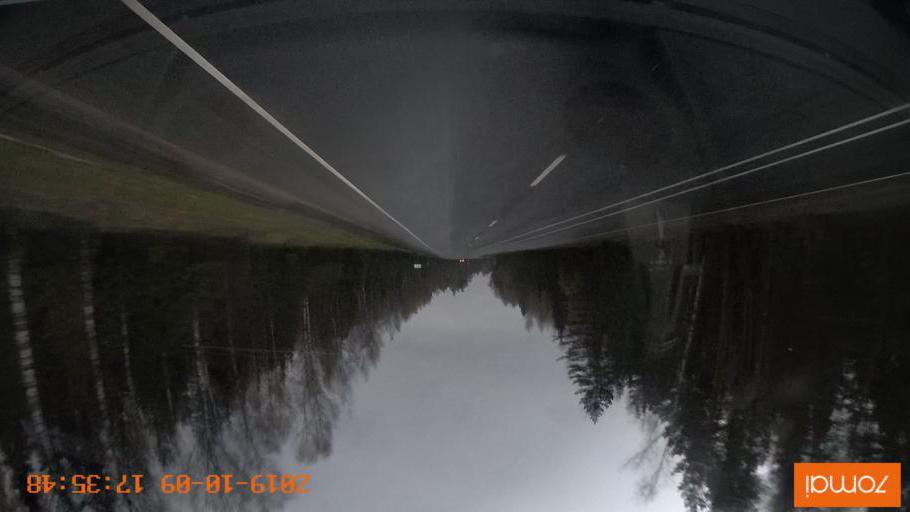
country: RU
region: Ivanovo
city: Bogorodskoye
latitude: 57.0880
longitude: 40.9996
